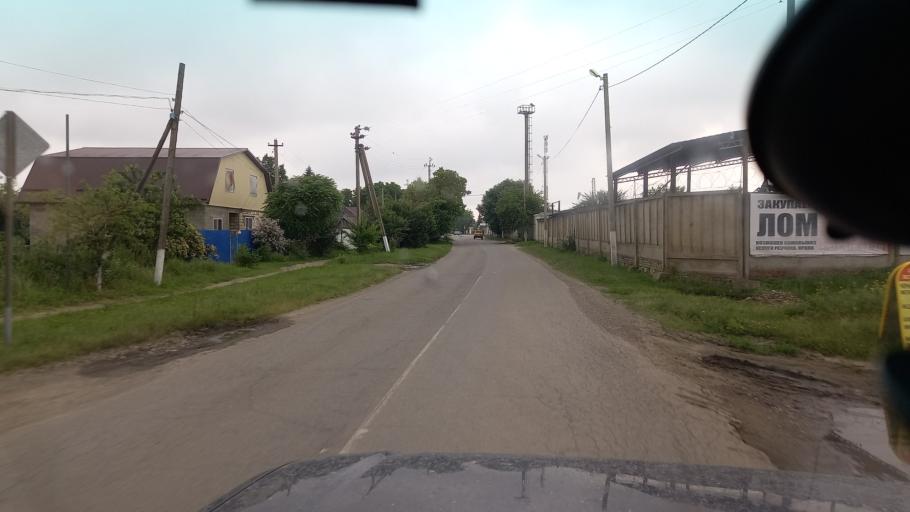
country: RU
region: Krasnodarskiy
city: Mostovskoy
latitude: 44.4195
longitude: 40.7767
